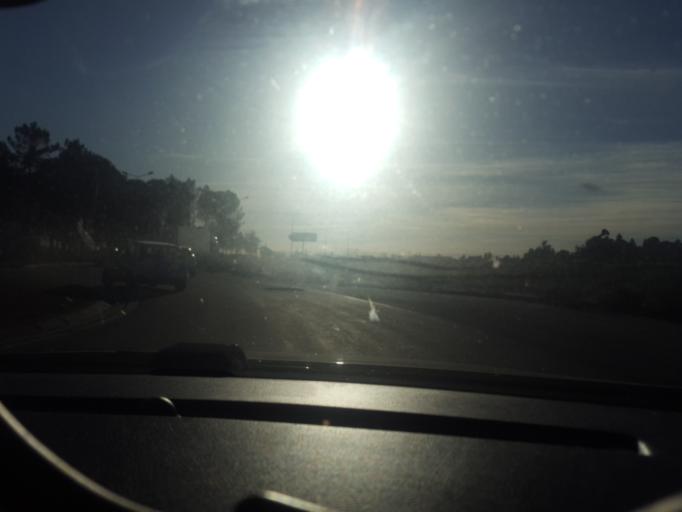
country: PT
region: Viseu
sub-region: Nelas
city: Nelas
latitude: 40.5426
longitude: -7.8452
